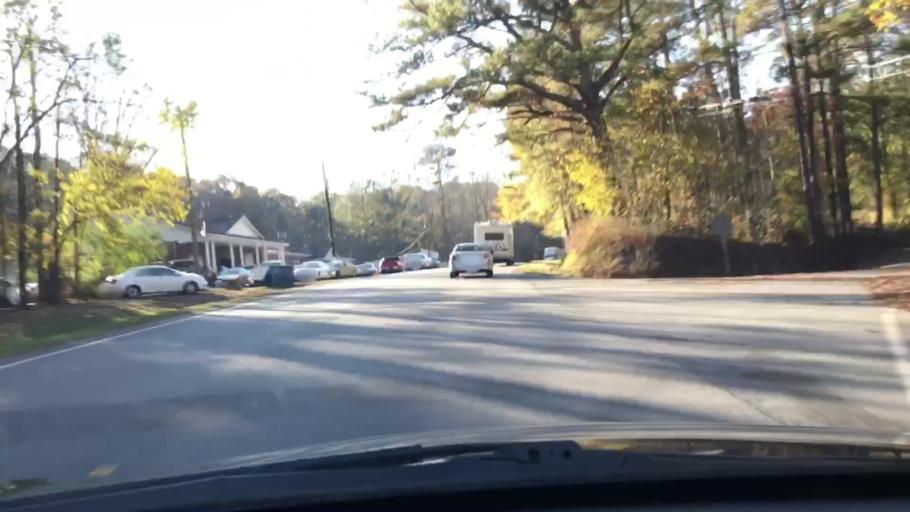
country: US
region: Alabama
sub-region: Cleburne County
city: Heflin
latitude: 33.6541
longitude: -85.5625
